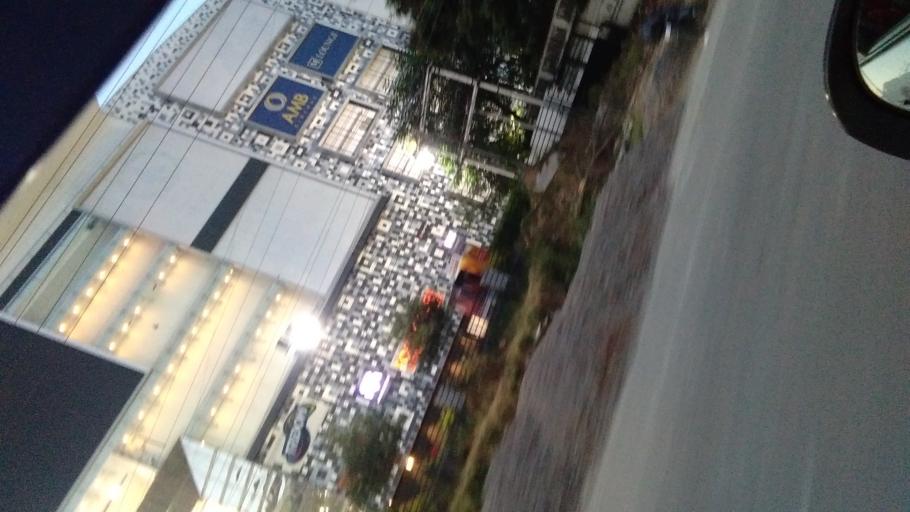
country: IN
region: Telangana
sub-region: Rangareddi
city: Kukatpalli
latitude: 17.4572
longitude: 78.3649
